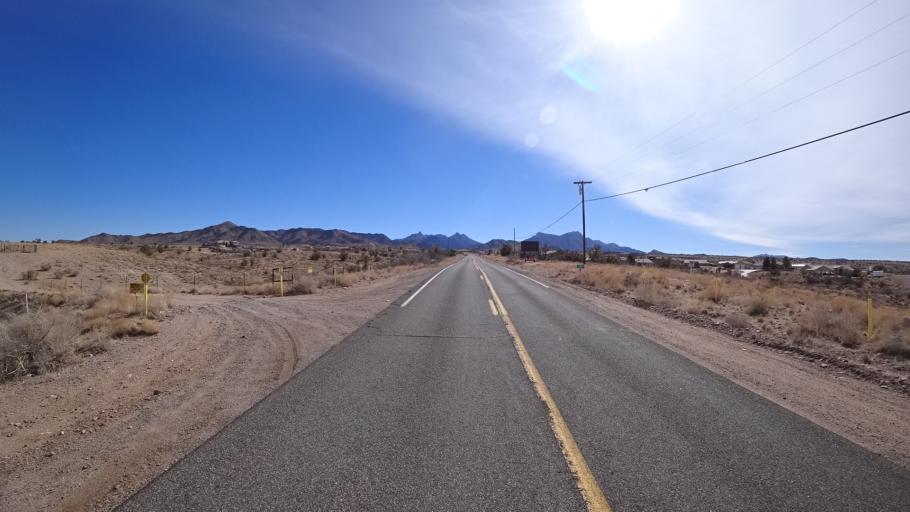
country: US
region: Arizona
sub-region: Mohave County
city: Kingman
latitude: 35.1735
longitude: -113.9847
